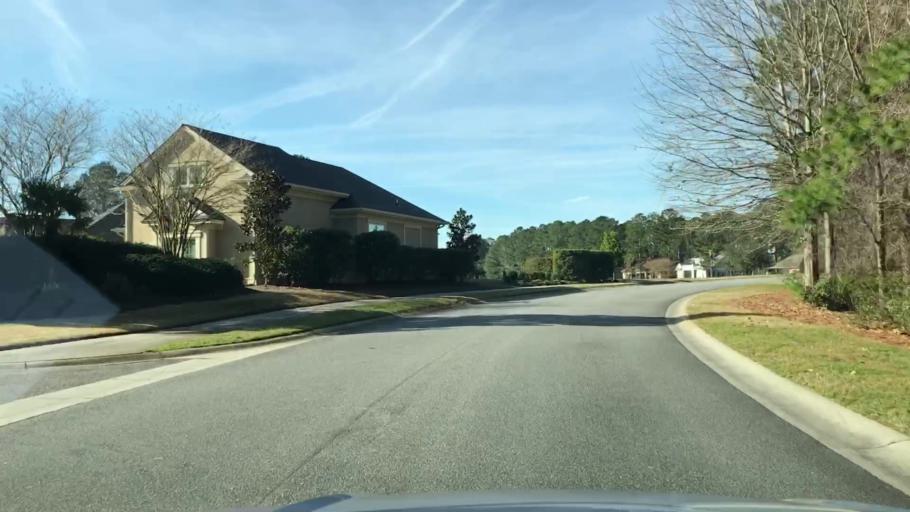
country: US
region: South Carolina
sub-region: Beaufort County
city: Bluffton
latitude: 32.2561
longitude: -80.9049
